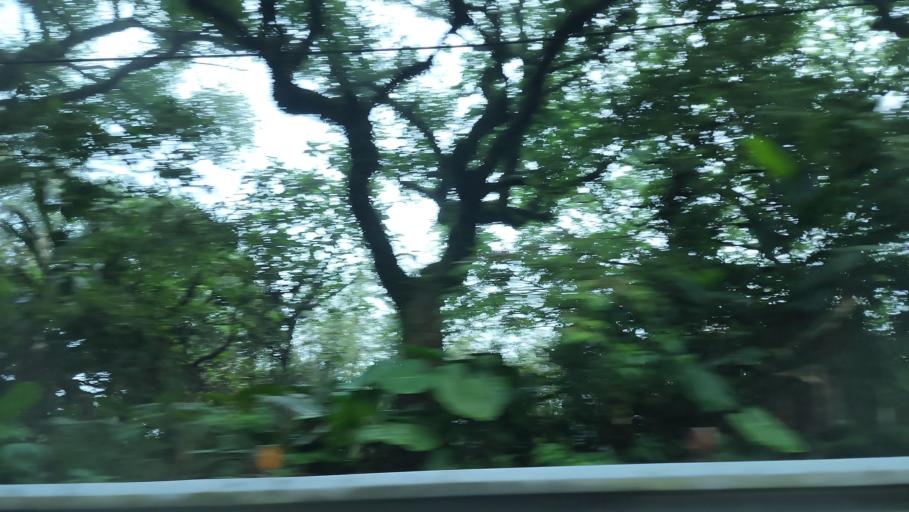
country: TW
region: Taipei
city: Taipei
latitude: 25.1450
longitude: 121.6041
